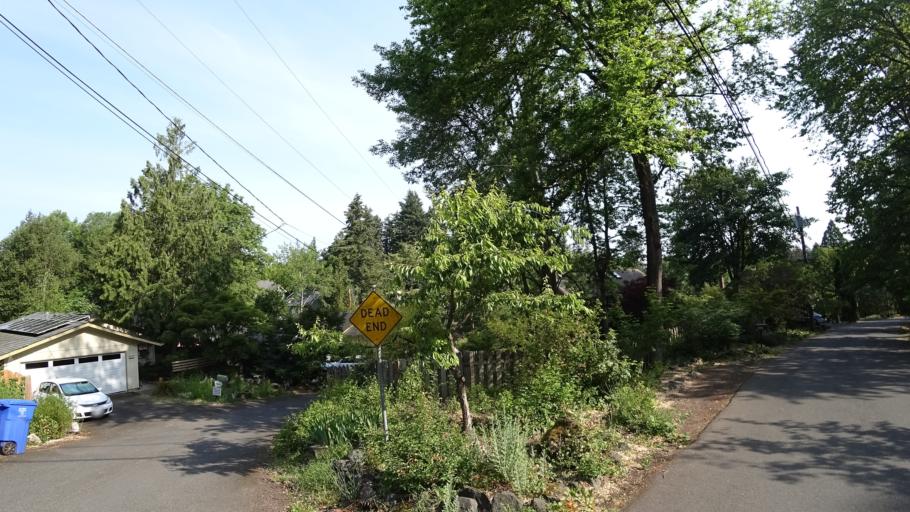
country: US
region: Oregon
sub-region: Washington County
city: Garden Home-Whitford
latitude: 45.4622
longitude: -122.7153
